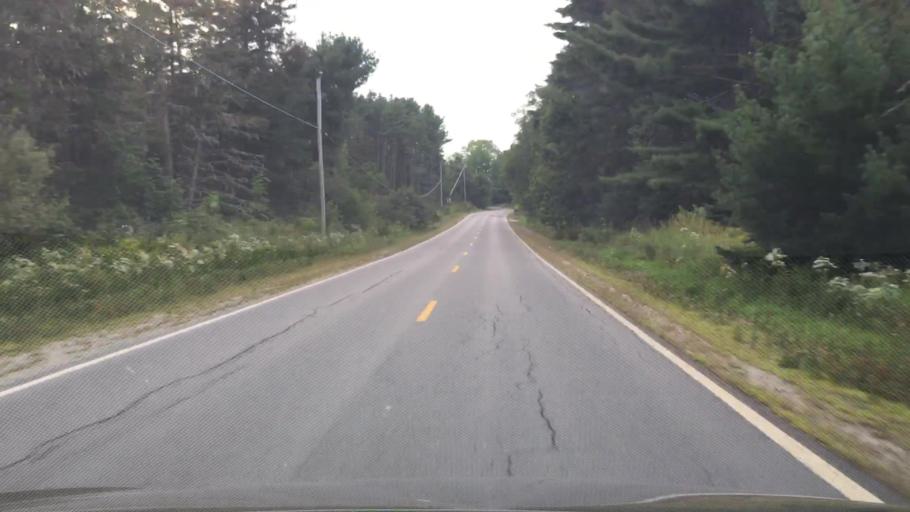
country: US
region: Maine
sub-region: Hancock County
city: Penobscot
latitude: 44.4510
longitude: -68.6972
